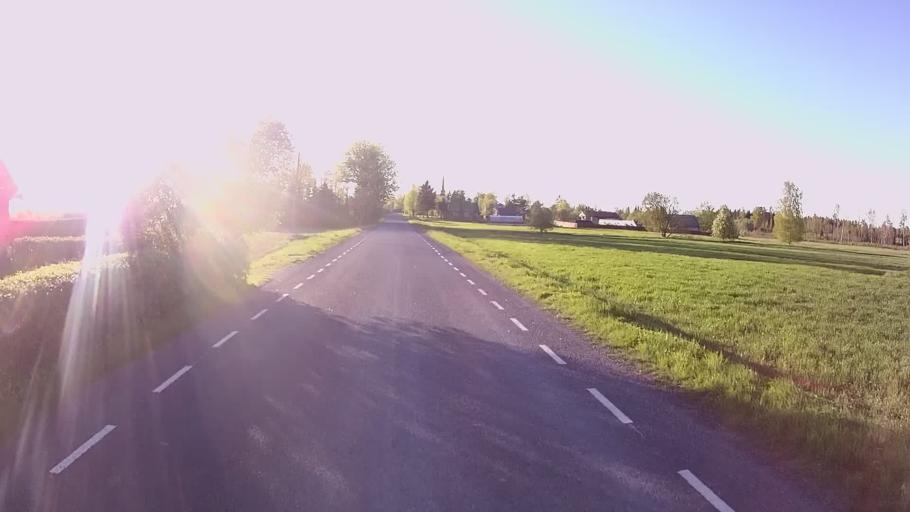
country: EE
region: Jogevamaa
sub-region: Poltsamaa linn
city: Poltsamaa
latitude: 58.5285
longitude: 25.9519
